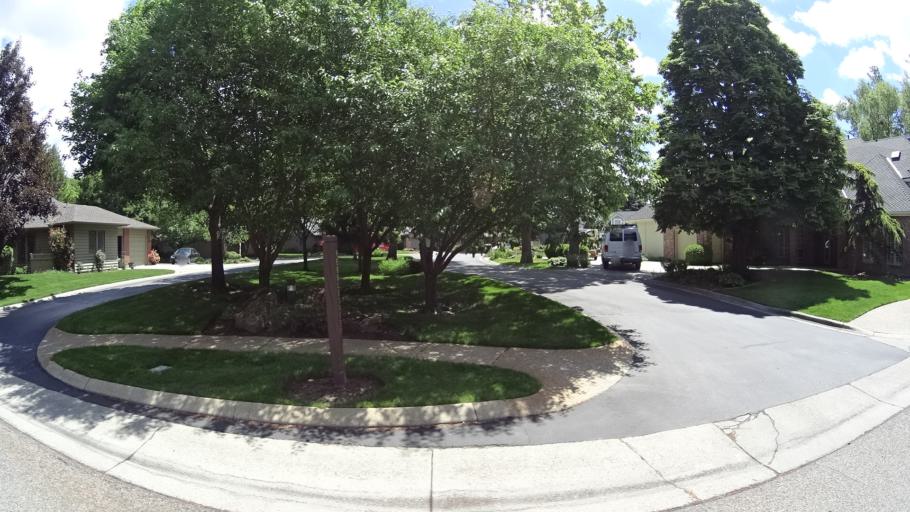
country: US
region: Idaho
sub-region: Ada County
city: Boise
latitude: 43.5861
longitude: -116.1659
